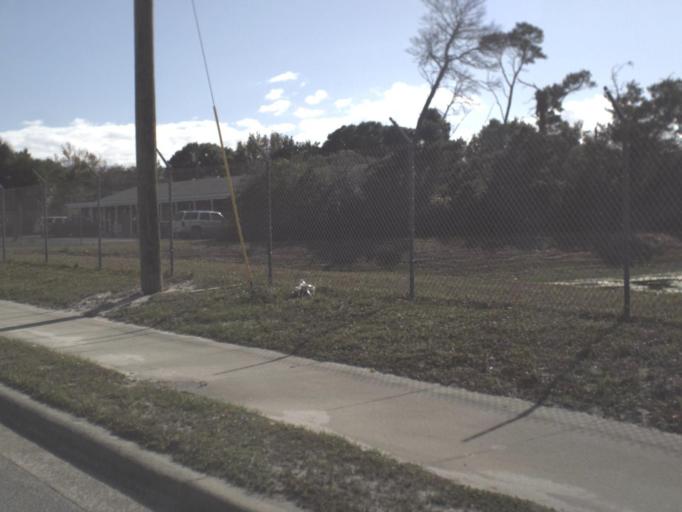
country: US
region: Florida
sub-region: Volusia County
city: Port Orange
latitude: 29.1348
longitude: -81.0308
